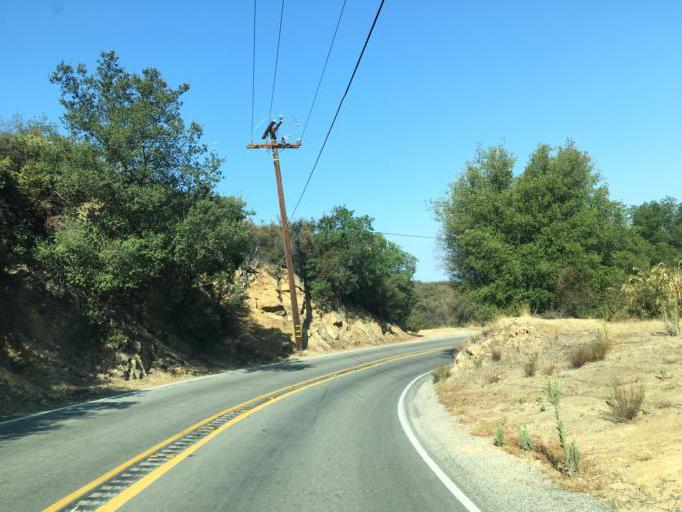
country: US
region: California
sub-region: Los Angeles County
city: Las Flores
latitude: 34.0850
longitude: -118.6564
